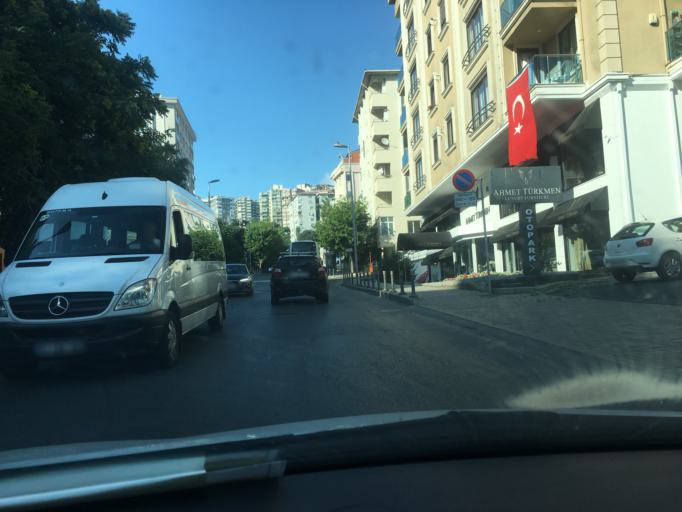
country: TR
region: Istanbul
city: Sisli
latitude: 41.0594
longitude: 29.0052
